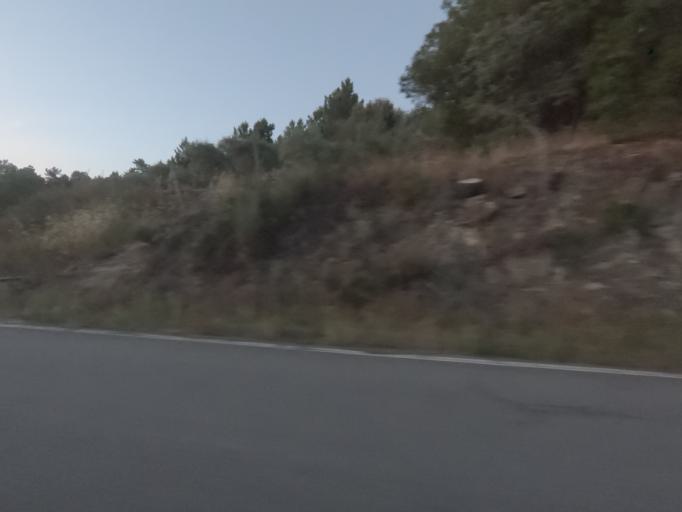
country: PT
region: Viseu
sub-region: Armamar
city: Armamar
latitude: 41.2001
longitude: -7.6971
